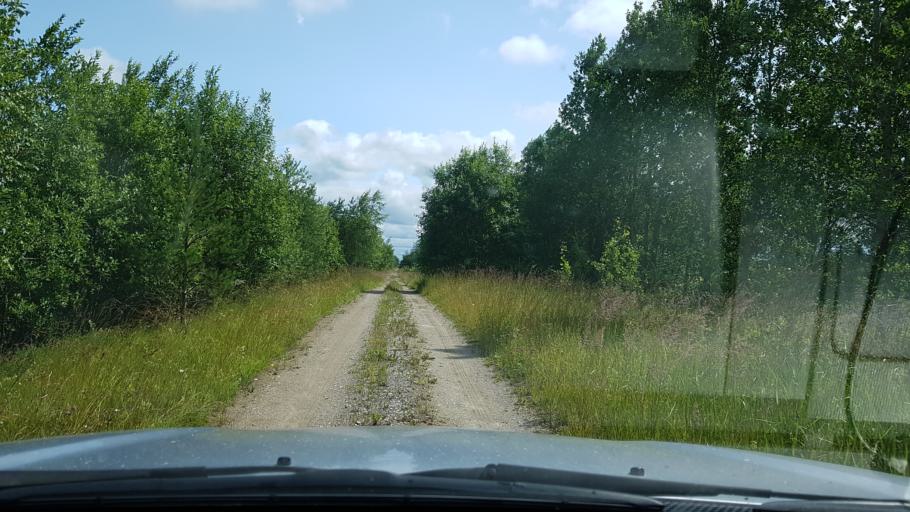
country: EE
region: Ida-Virumaa
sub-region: Sillamaee linn
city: Sillamae
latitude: 59.3622
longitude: 27.7953
